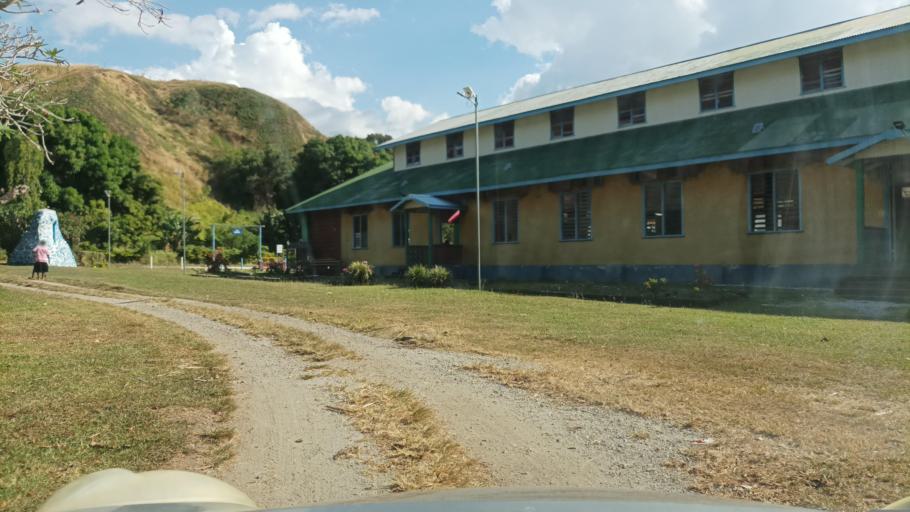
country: SB
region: Guadalcanal
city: Honiara
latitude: -9.2529
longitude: 159.6955
